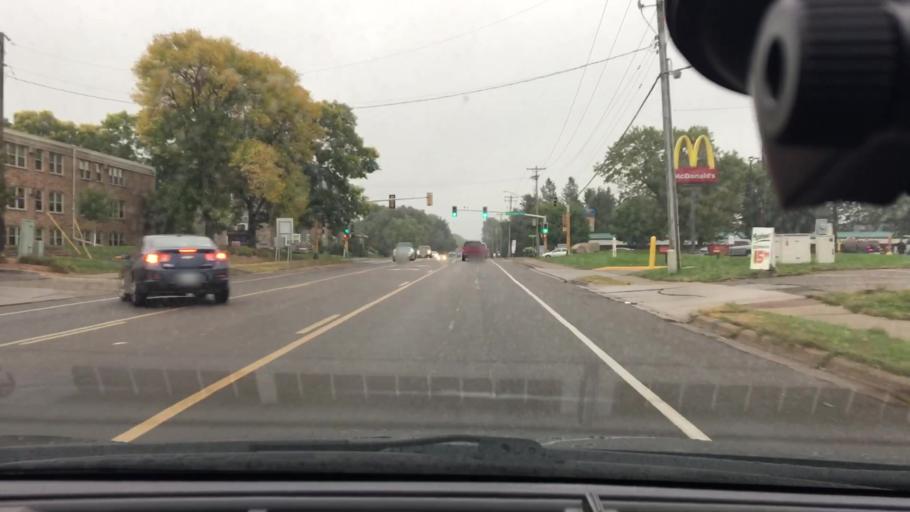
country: US
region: Minnesota
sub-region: Hennepin County
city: New Hope
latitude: 45.0075
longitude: -93.3993
